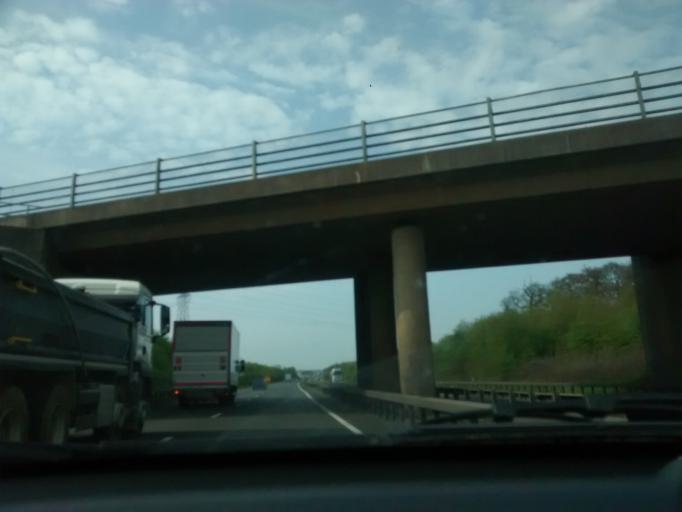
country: GB
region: England
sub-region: Oxfordshire
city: Kidlington
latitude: 51.8040
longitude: -1.2755
